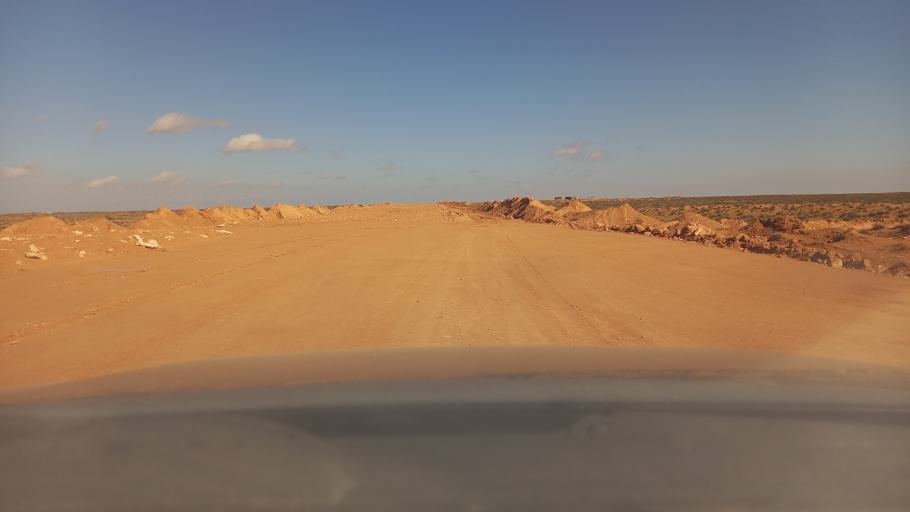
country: TN
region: Madanin
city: Medenine
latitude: 33.2415
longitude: 10.5566
